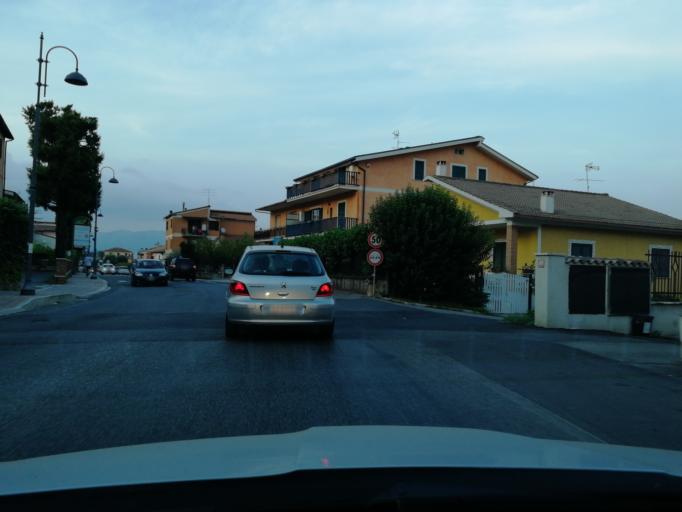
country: IT
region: Latium
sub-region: Citta metropolitana di Roma Capitale
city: Artena
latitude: 41.7426
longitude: 12.9149
